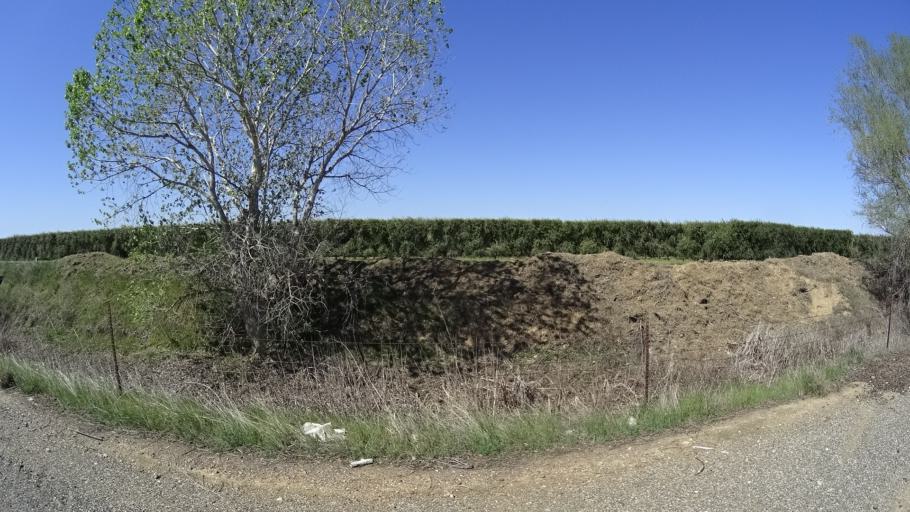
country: US
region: California
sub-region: Glenn County
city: Orland
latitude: 39.6494
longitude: -122.2533
